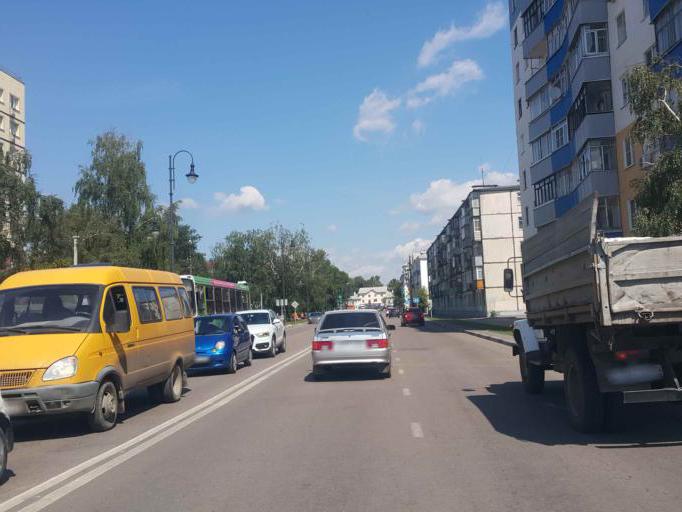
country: RU
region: Tambov
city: Tambov
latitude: 52.7375
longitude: 41.4477
